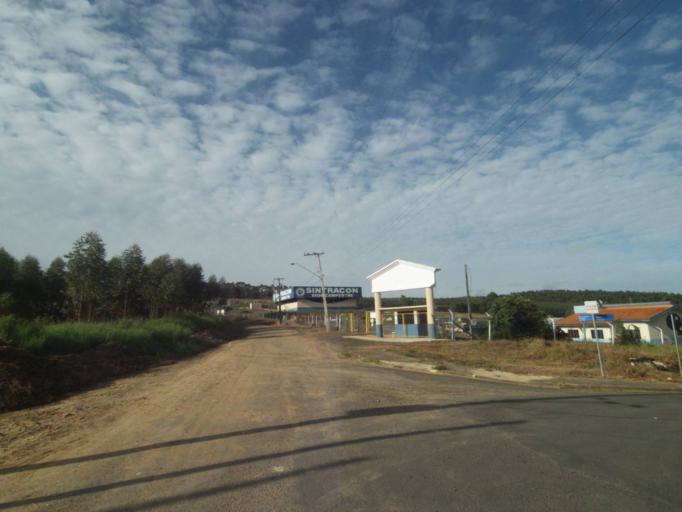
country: BR
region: Parana
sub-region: Telemaco Borba
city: Telemaco Borba
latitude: -24.3486
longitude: -50.6131
